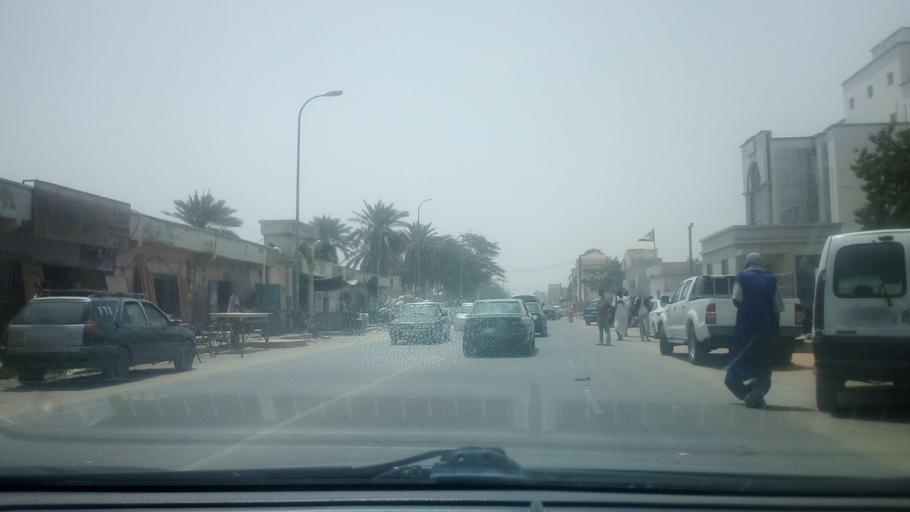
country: MR
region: Nouakchott
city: Nouakchott
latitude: 18.0839
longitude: -15.9905
